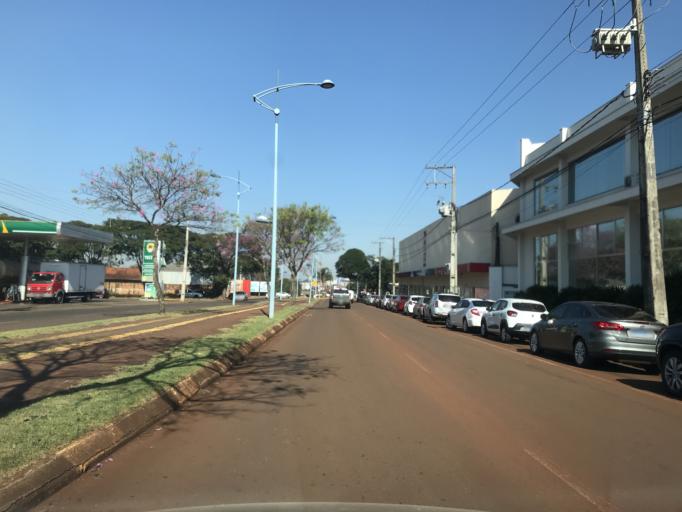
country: BR
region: Parana
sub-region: Toledo
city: Toledo
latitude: -24.7244
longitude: -53.7231
